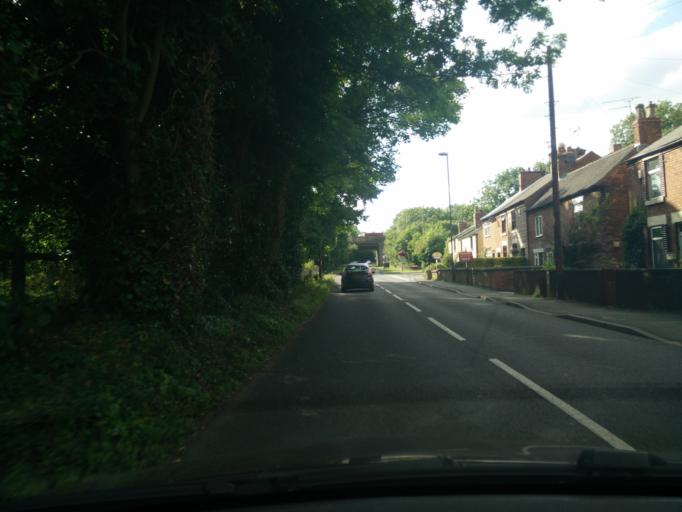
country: GB
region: England
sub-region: Derbyshire
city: Kilburn
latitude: 53.0135
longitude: -1.4402
